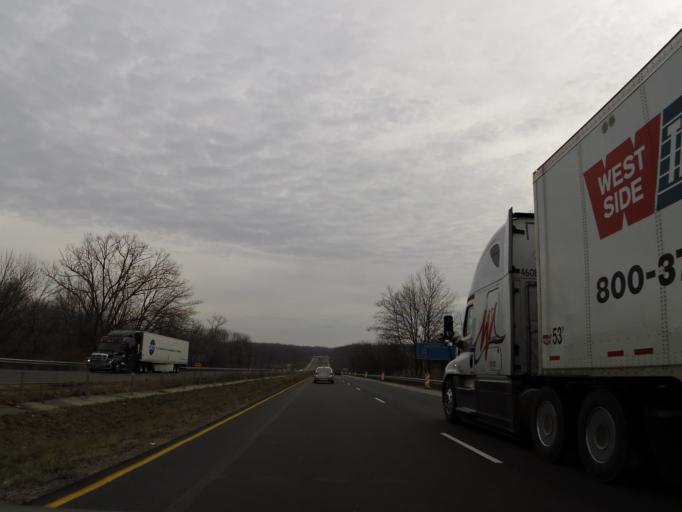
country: US
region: Illinois
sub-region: Vermilion County
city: Oakwood
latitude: 40.1275
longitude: -87.7382
